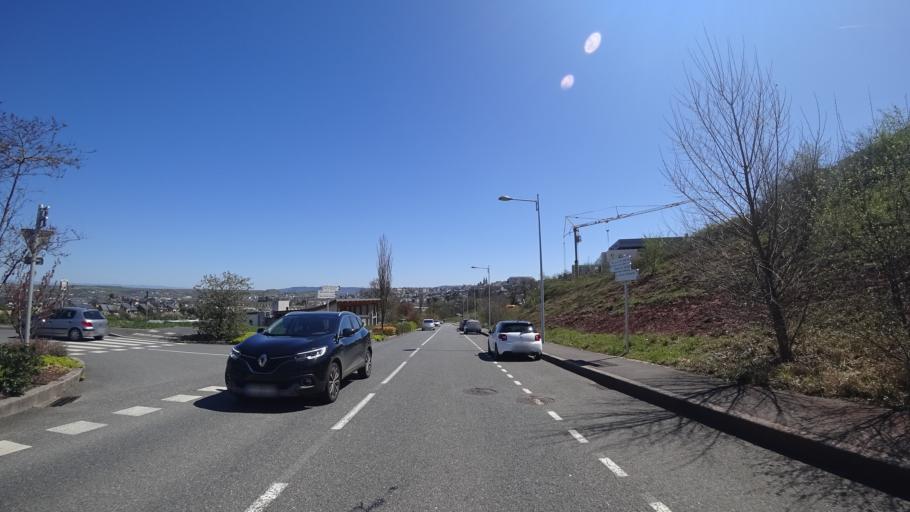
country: FR
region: Midi-Pyrenees
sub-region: Departement de l'Aveyron
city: Rodez
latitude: 44.3612
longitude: 2.5592
